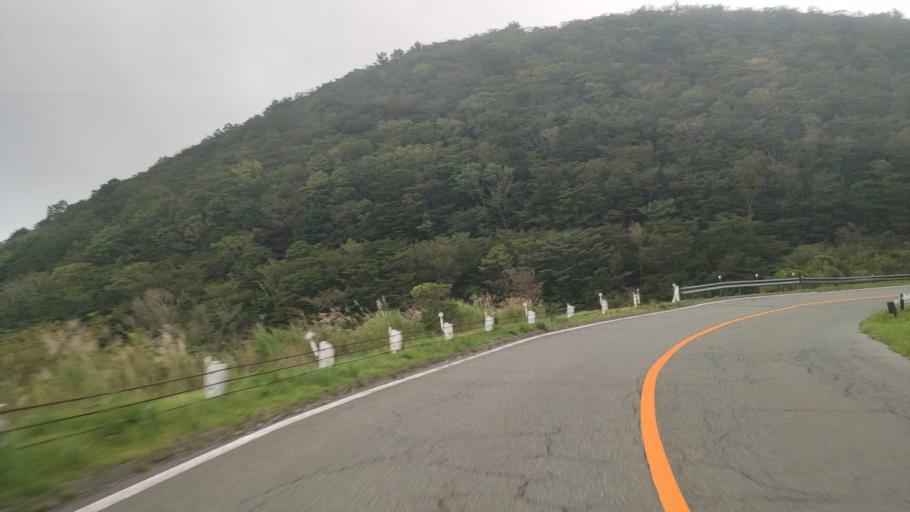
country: JP
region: Shizuoka
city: Gotemba
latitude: 35.2909
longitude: 138.7809
